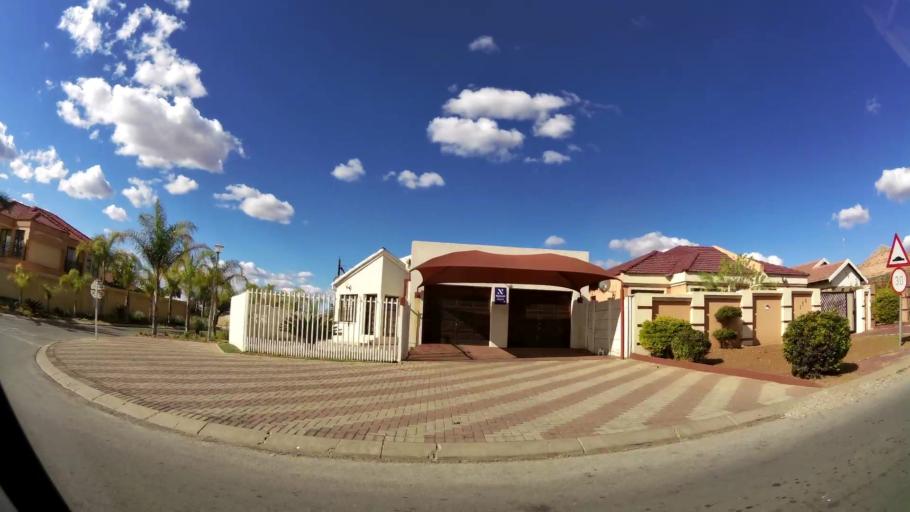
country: ZA
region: Limpopo
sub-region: Capricorn District Municipality
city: Polokwane
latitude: -23.8833
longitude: 29.4740
